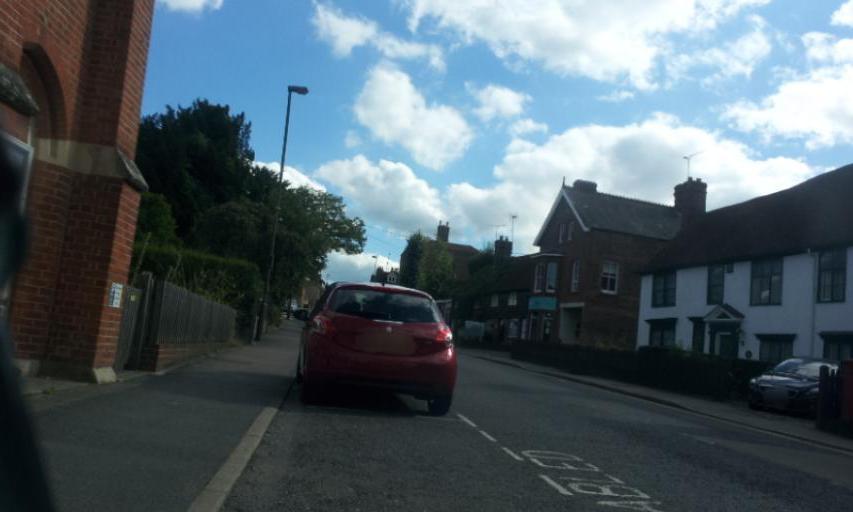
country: GB
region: England
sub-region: Kent
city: Staplehurst
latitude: 51.1600
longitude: 0.5524
